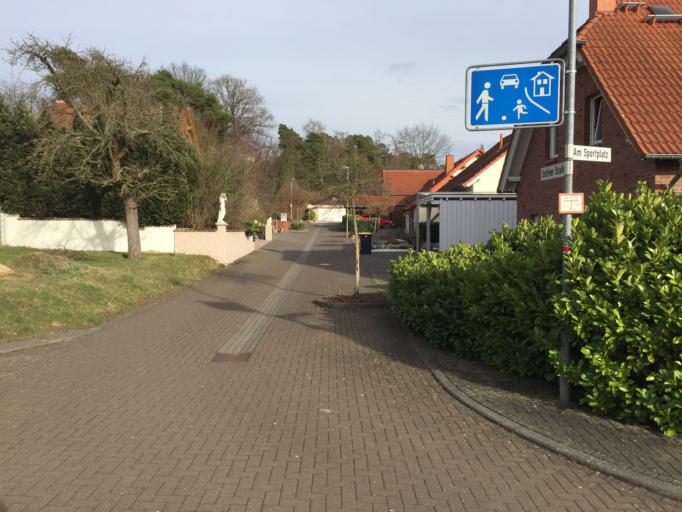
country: DE
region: Hesse
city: Beuern
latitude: 50.6710
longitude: 8.7870
